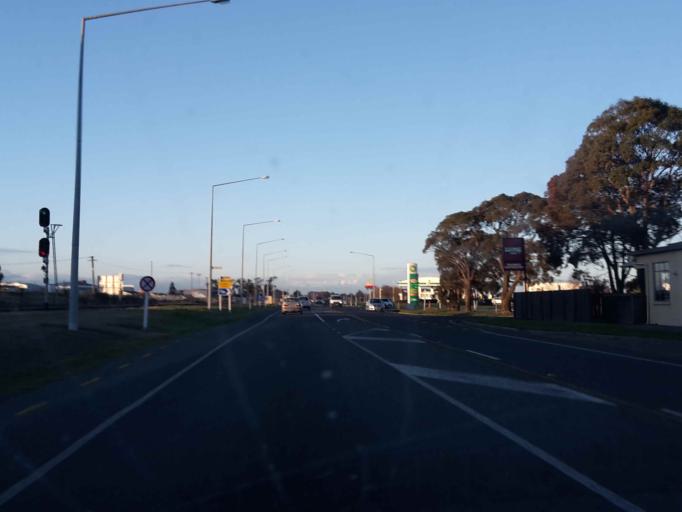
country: NZ
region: Canterbury
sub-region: Selwyn District
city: Rolleston
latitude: -43.5913
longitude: 172.3773
